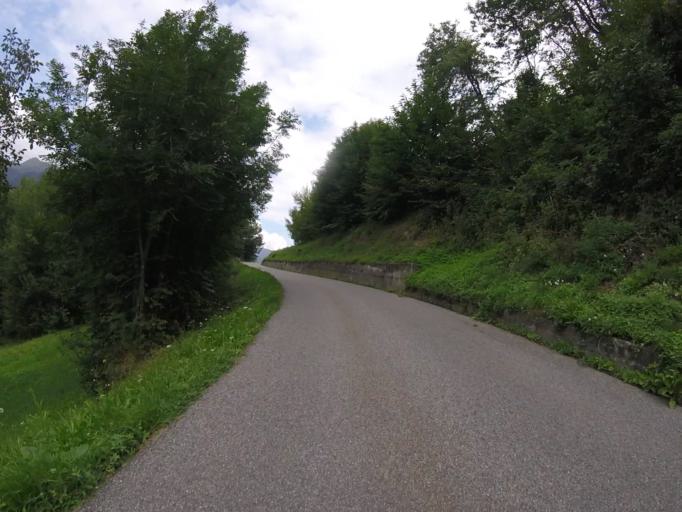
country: IT
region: Lombardy
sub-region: Provincia di Sondrio
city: Mazzo di Valtellina
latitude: 46.2600
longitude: 10.2670
